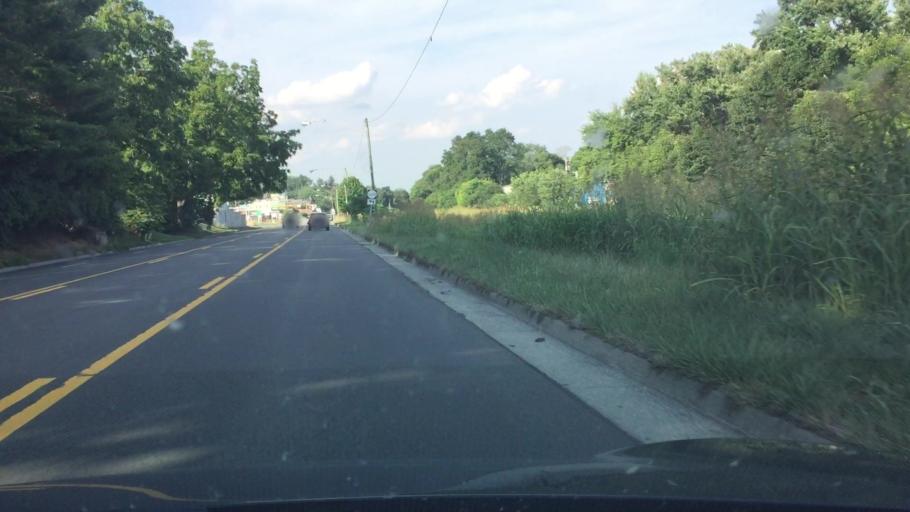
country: US
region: Virginia
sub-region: Pulaski County
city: Dublin
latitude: 37.1077
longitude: -80.6820
